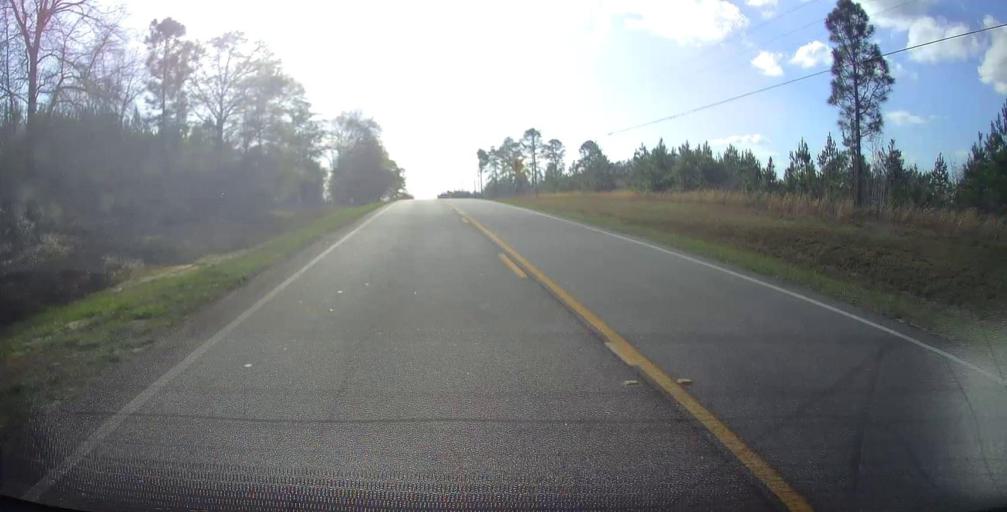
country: US
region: Georgia
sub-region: Wheeler County
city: Alamo
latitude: 32.1592
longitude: -82.7395
